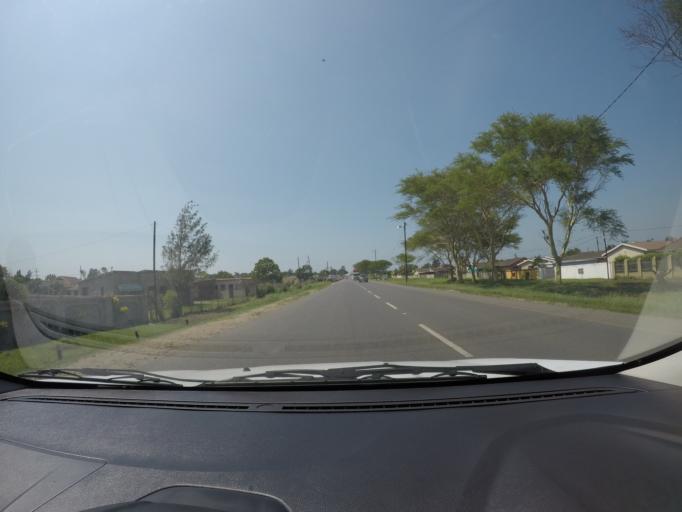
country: ZA
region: KwaZulu-Natal
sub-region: uThungulu District Municipality
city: eSikhawini
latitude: -28.8612
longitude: 31.9245
